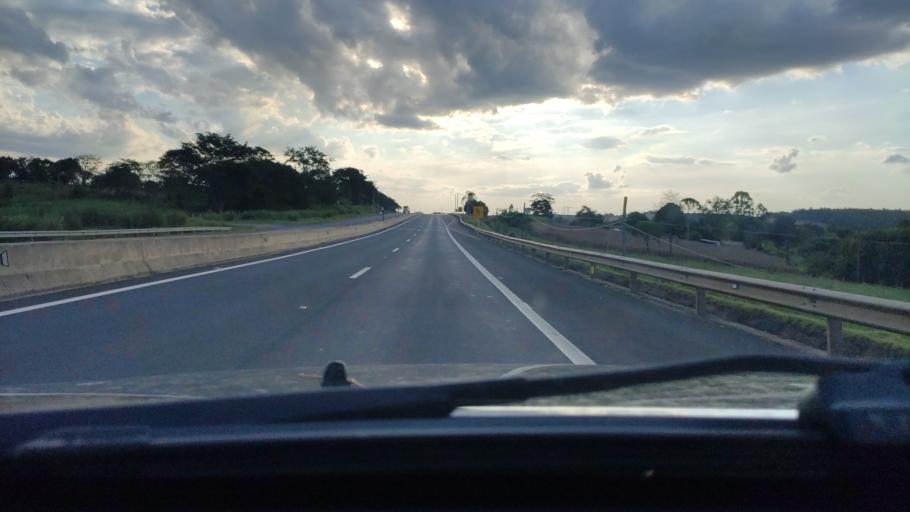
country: BR
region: Sao Paulo
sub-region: Mogi-Mirim
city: Mogi Mirim
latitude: -22.4426
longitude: -47.0415
